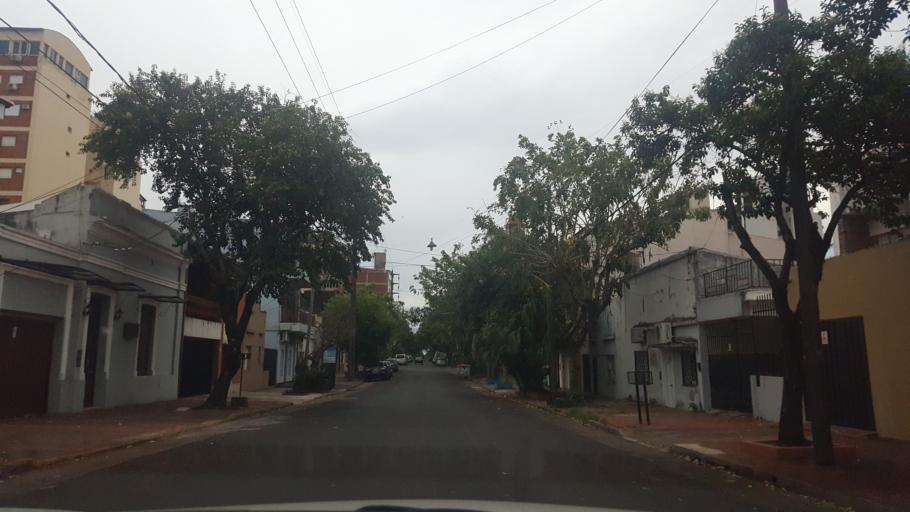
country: AR
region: Misiones
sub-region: Departamento de Capital
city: Posadas
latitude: -27.3694
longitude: -55.8886
